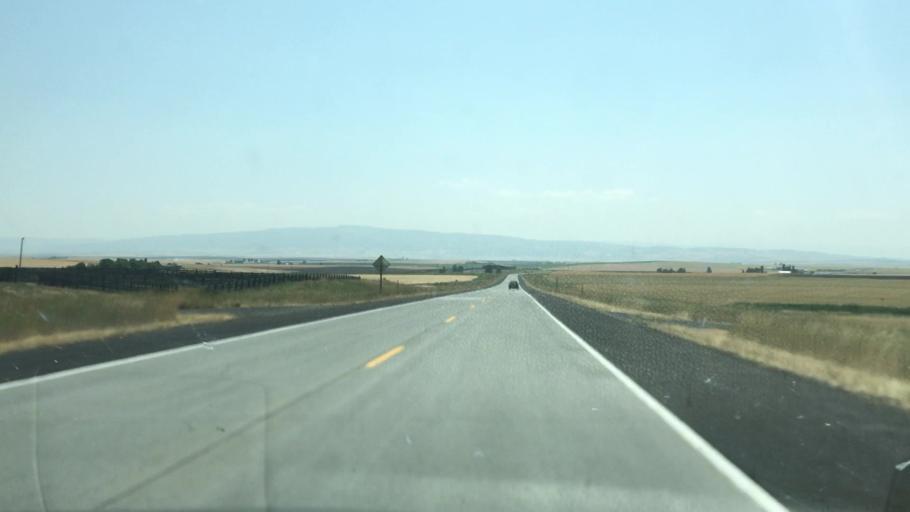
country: US
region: Idaho
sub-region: Lewis County
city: Nezperce
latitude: 46.0340
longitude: -116.3350
